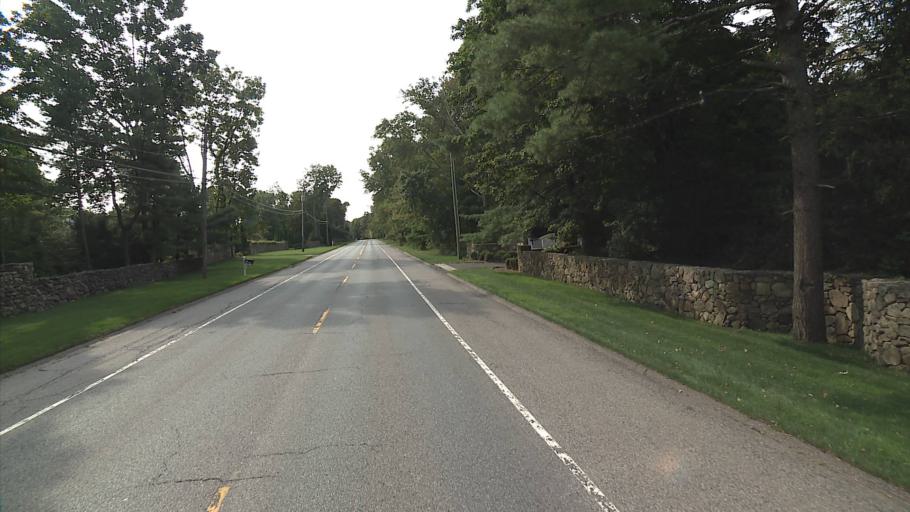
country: US
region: Connecticut
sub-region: Fairfield County
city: New Canaan
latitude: 41.1906
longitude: -73.5062
